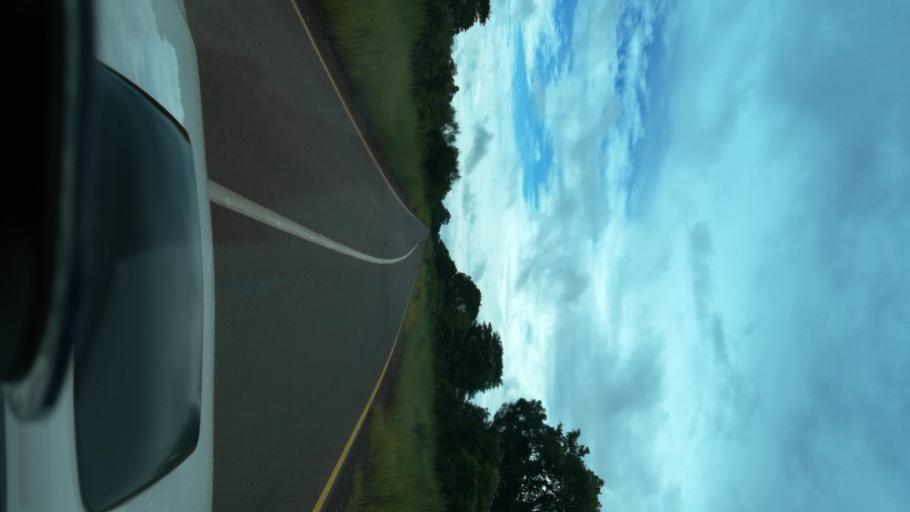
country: ZM
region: Luapula
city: Mwense
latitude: -10.7731
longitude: 28.2569
